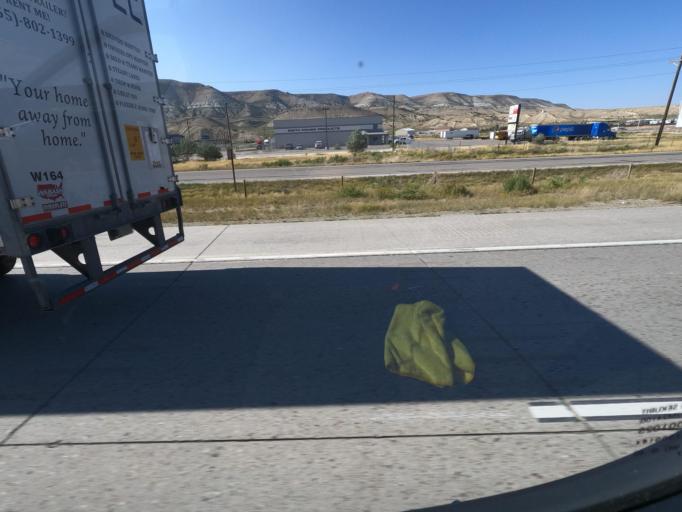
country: US
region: Wyoming
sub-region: Sweetwater County
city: North Rock Springs
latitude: 41.5648
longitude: -109.2938
